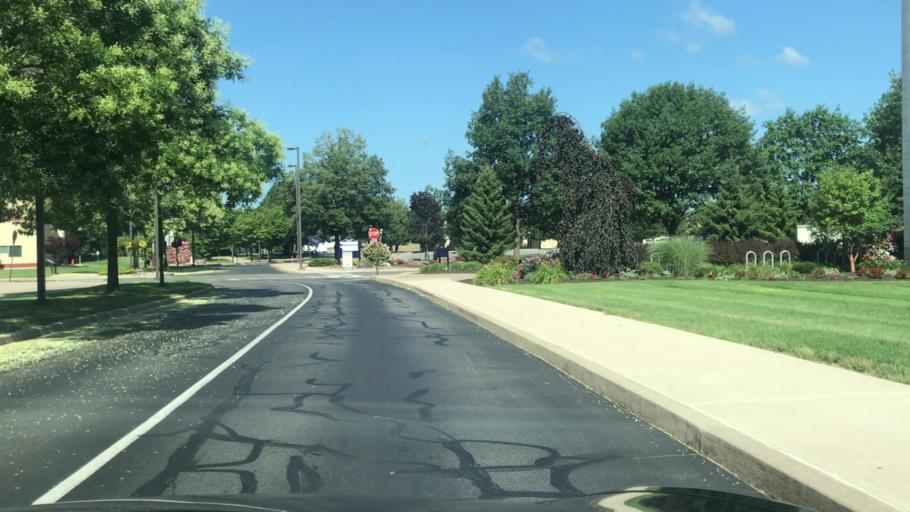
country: US
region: Pennsylvania
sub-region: Lycoming County
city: Duboistown
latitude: 41.2352
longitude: -77.0221
